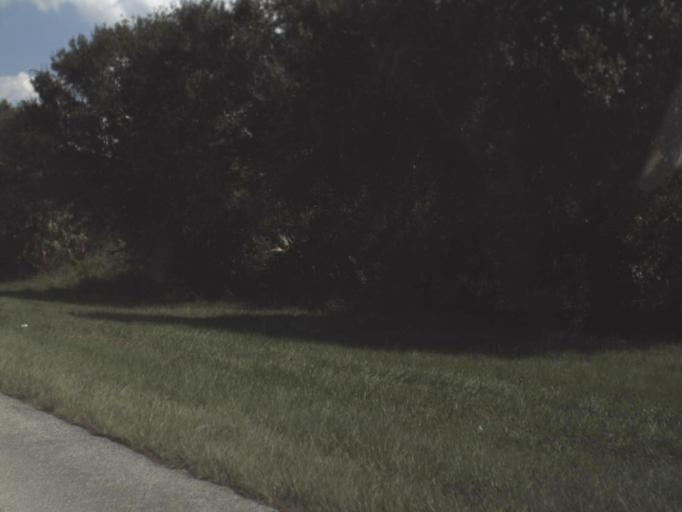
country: US
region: Florida
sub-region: Highlands County
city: Sebring
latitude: 27.4417
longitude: -81.3011
